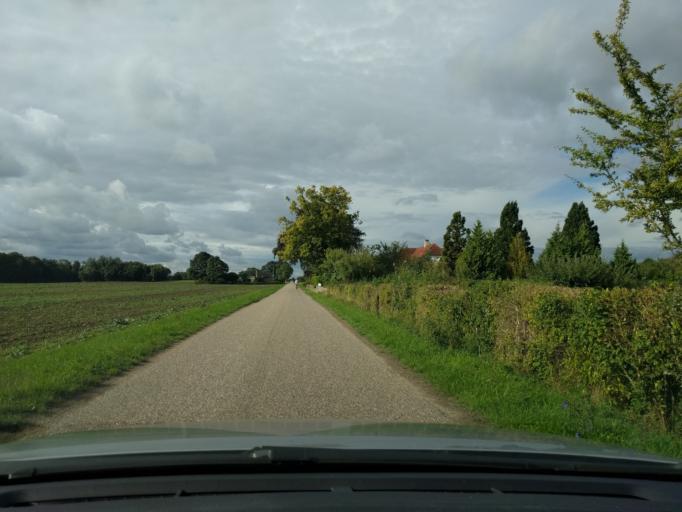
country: DK
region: South Denmark
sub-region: Kerteminde Kommune
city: Kerteminde
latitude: 55.4055
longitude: 10.6554
